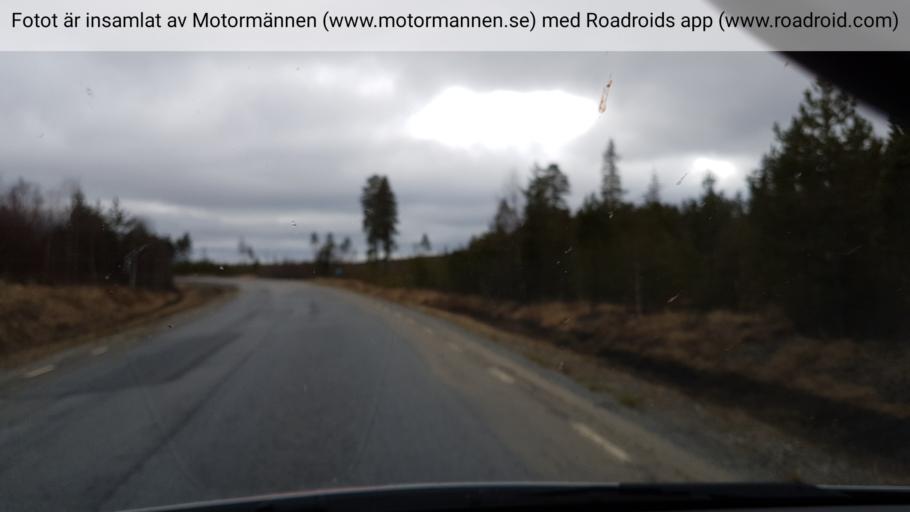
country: SE
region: Vaesterbotten
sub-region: Lycksele Kommun
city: Lycksele
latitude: 63.9887
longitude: 18.4790
